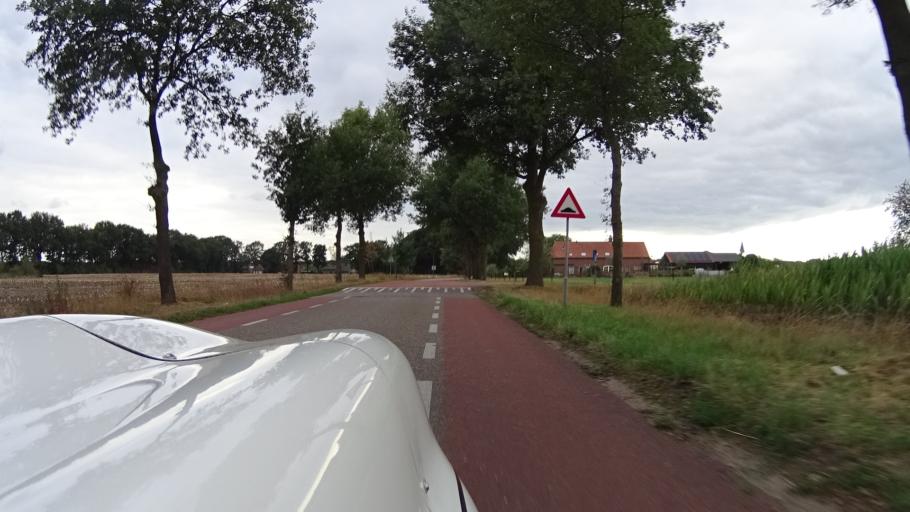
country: NL
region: North Brabant
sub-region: Gemeente Maasdonk
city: Geffen
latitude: 51.6929
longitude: 5.4613
